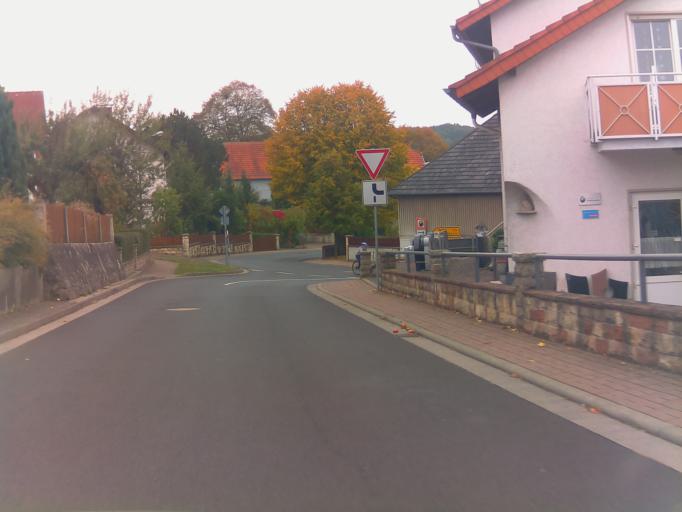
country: DE
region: Hesse
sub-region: Regierungsbezirk Kassel
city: Eichenzell
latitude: 50.4659
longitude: 9.6789
